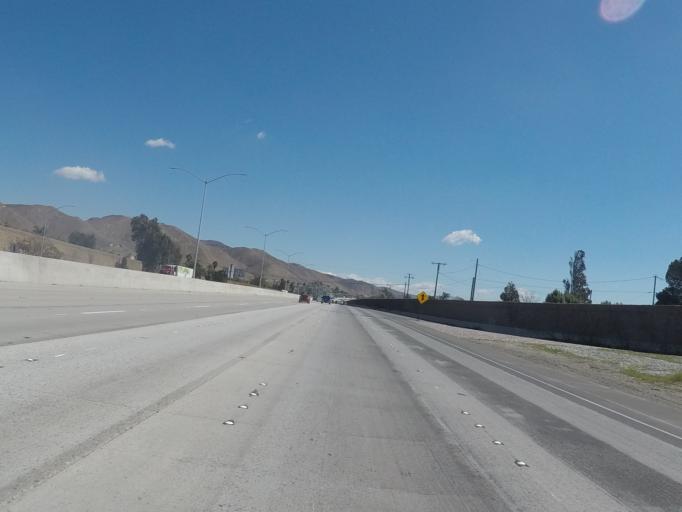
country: US
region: California
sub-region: Riverside County
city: Glen Avon
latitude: 34.0188
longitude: -117.5048
